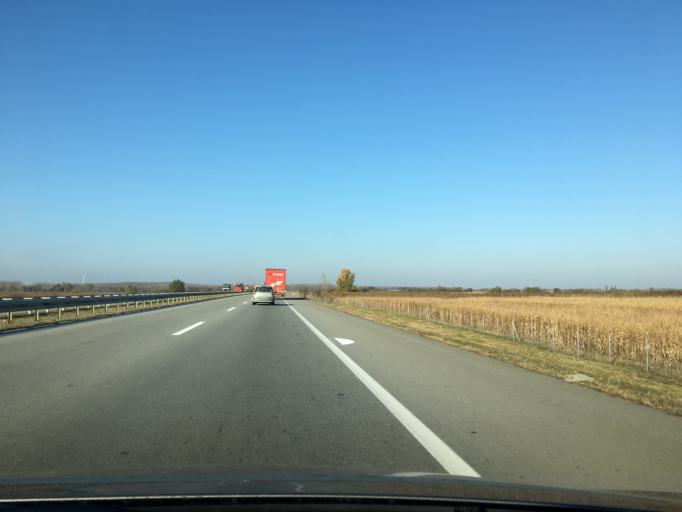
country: RS
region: Autonomna Pokrajina Vojvodina
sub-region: Juznobacki Okrug
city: Sremski Karlovci
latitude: 45.2674
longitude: 19.9609
